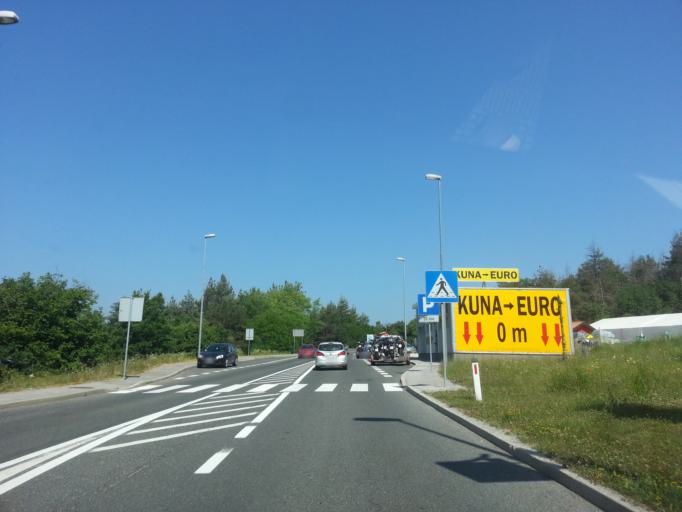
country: SI
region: Ilirska Bistrica
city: Ilirska Bistrica
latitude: 45.4925
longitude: 14.2754
